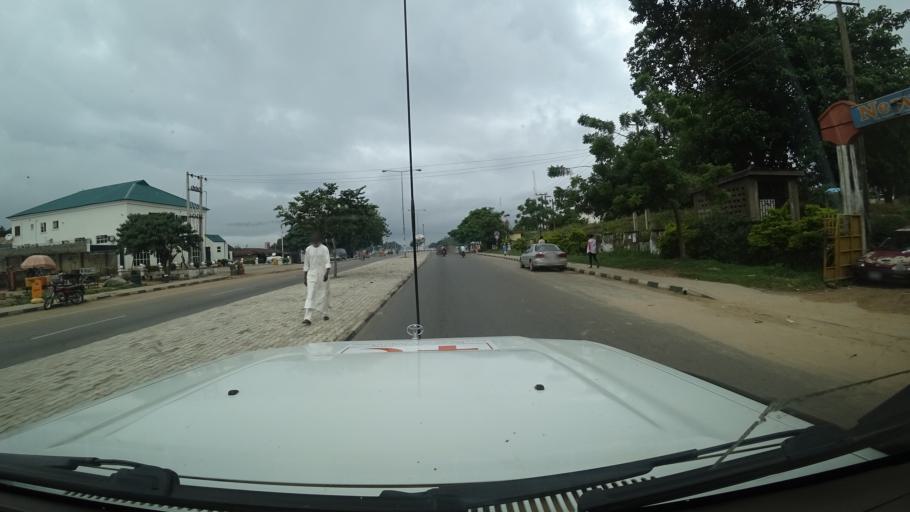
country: NG
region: Niger
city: Minna
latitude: 9.6033
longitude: 6.5575
